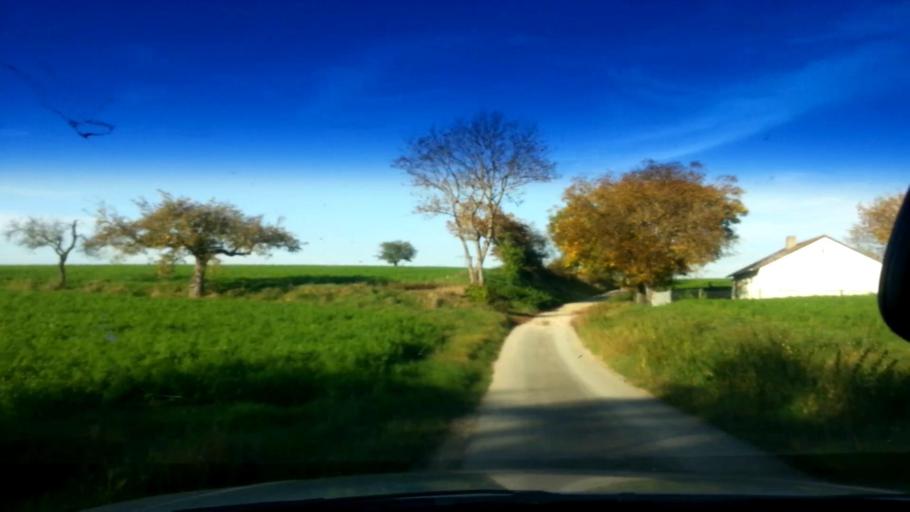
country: DE
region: Bavaria
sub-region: Upper Franconia
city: Litzendorf
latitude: 49.9140
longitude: 10.9900
